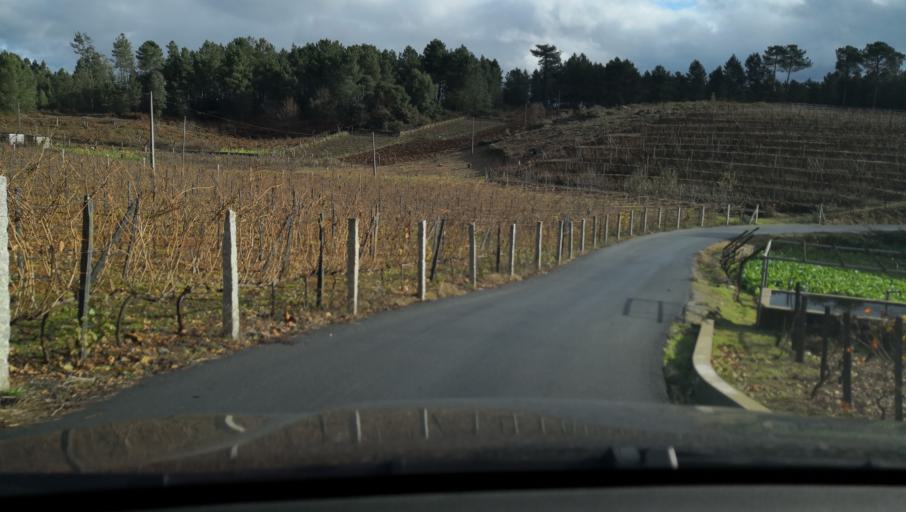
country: PT
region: Vila Real
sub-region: Vila Real
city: Vila Real
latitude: 41.2680
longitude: -7.7219
